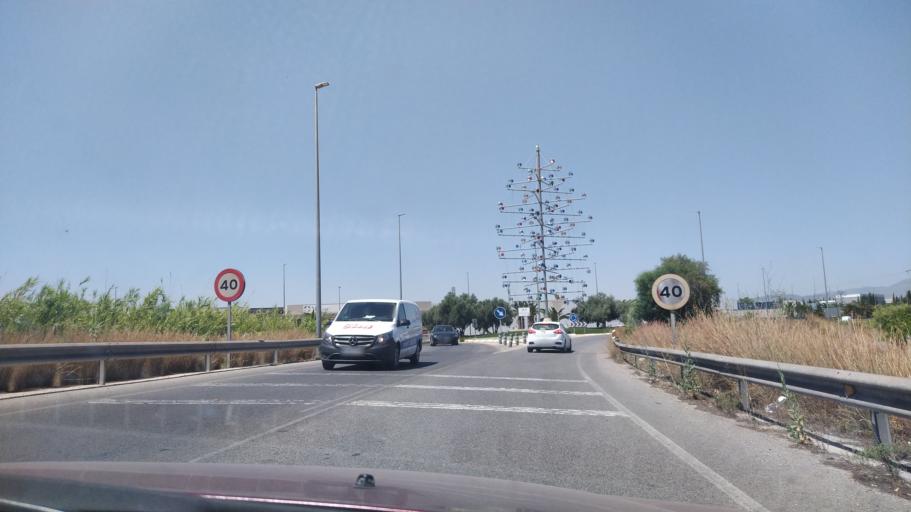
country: ES
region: Murcia
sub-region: Murcia
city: Lorqui
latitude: 38.0840
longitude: -1.2629
